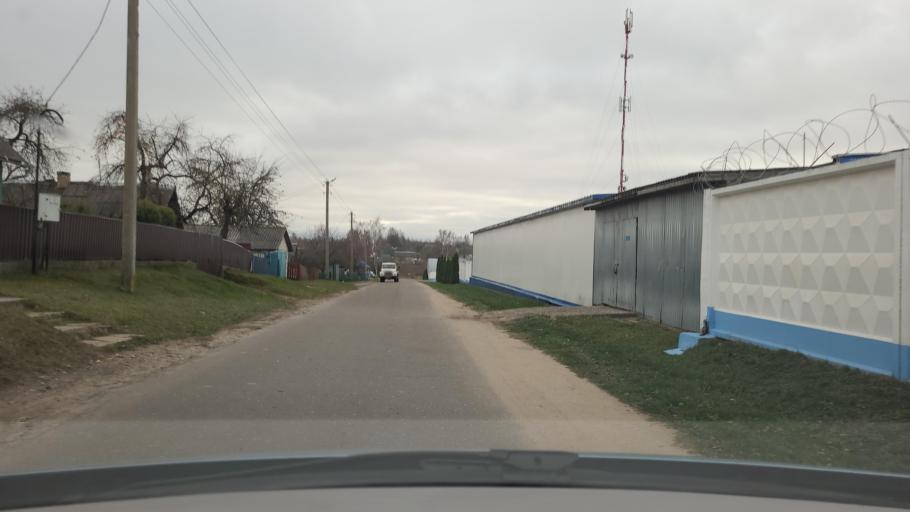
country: BY
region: Minsk
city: Khalopyenichy
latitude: 54.5157
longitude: 28.9549
